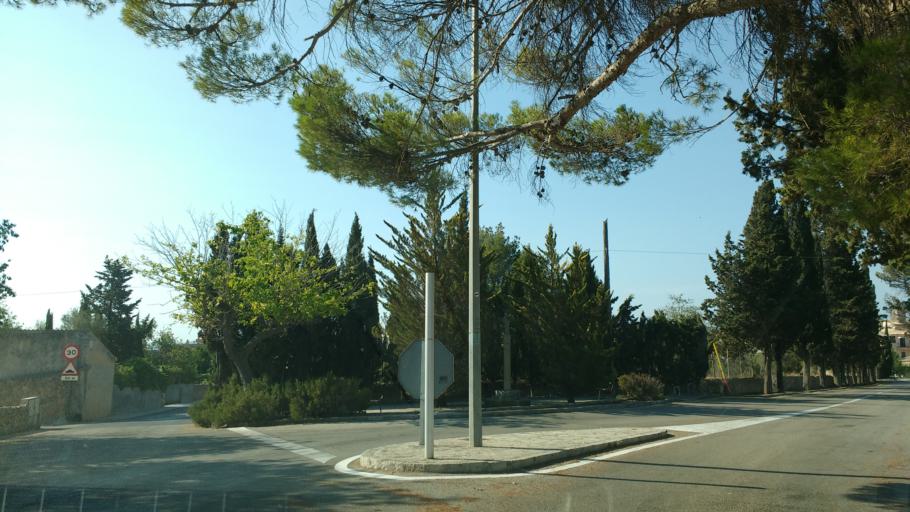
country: ES
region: Balearic Islands
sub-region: Illes Balears
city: Consell
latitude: 39.6720
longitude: 2.8147
